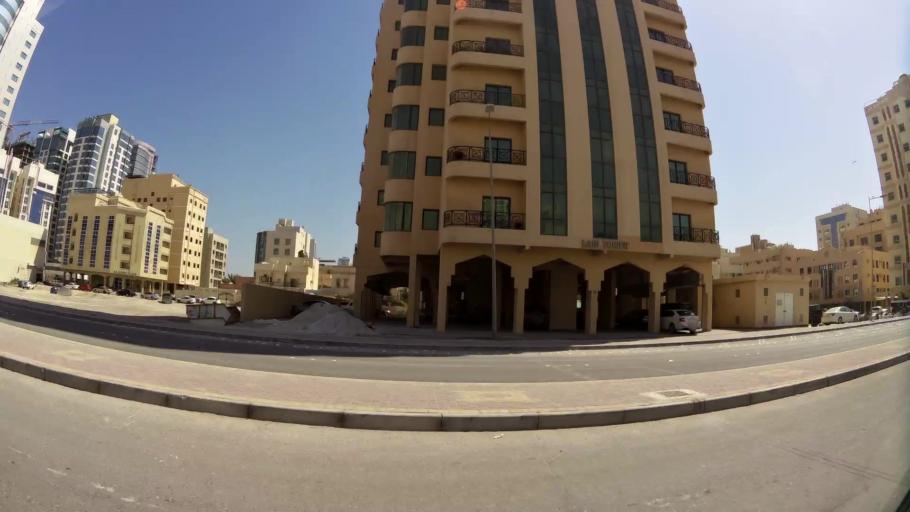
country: BH
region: Manama
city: Manama
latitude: 26.2129
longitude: 50.6098
